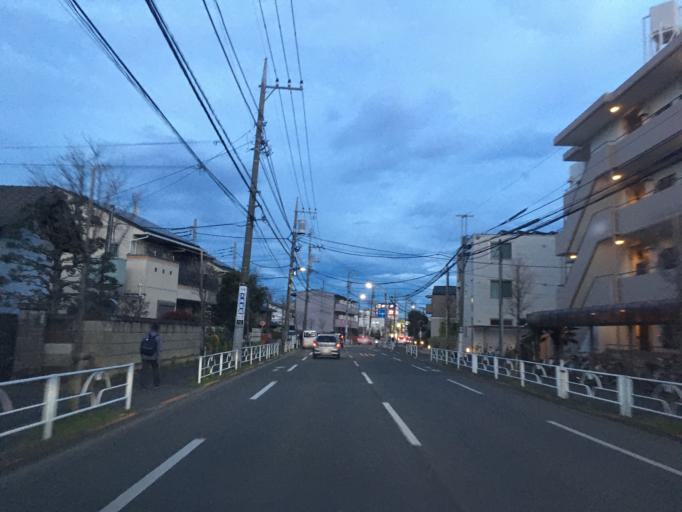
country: JP
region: Tokyo
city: Tanashicho
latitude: 35.7233
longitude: 139.5080
